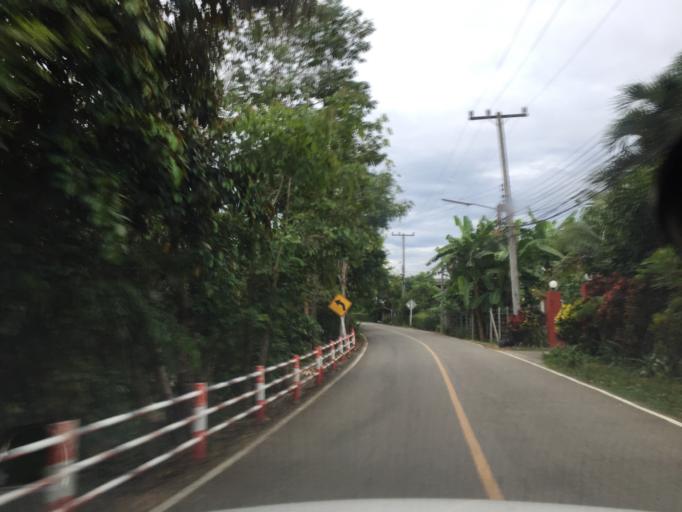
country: TH
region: Chiang Mai
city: Mae On
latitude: 18.8274
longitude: 99.1801
